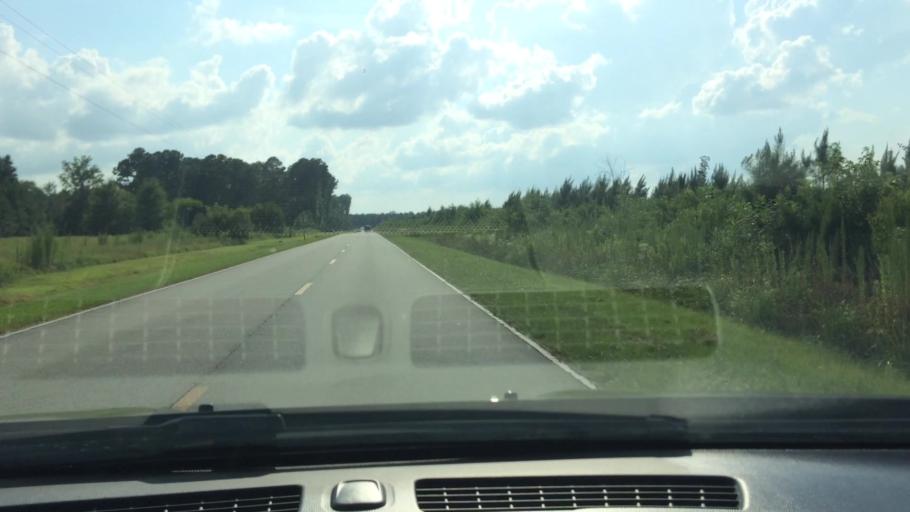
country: US
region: North Carolina
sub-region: Beaufort County
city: River Road
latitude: 35.4367
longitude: -77.0000
